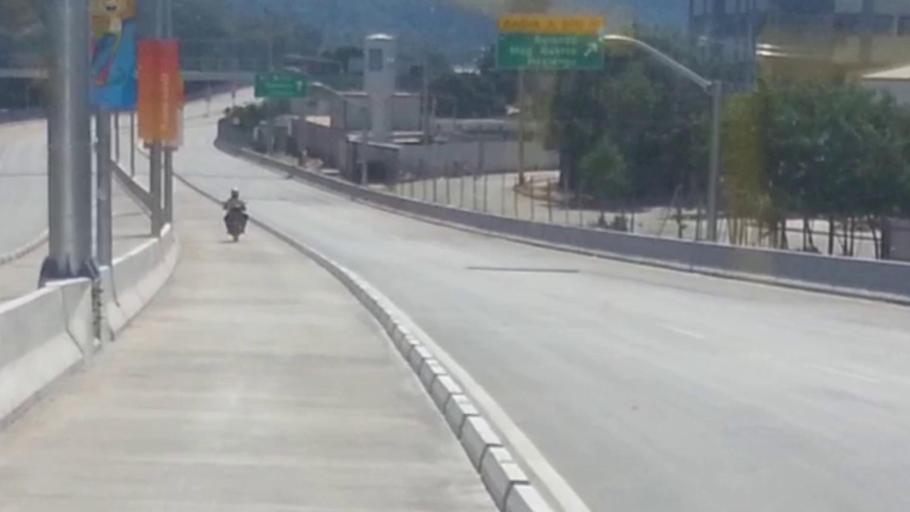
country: BR
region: Rio de Janeiro
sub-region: Nilopolis
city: Nilopolis
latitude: -22.8953
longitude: -43.3993
